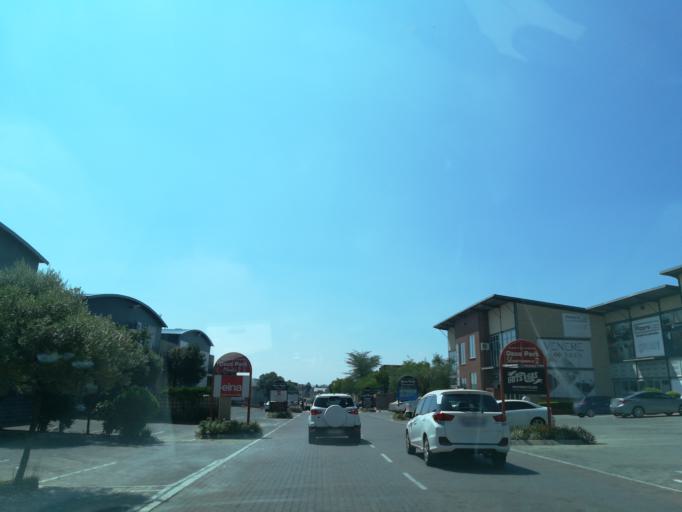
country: ZA
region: Gauteng
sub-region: City of Johannesburg Metropolitan Municipality
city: Diepsloot
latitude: -26.0362
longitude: 27.9575
